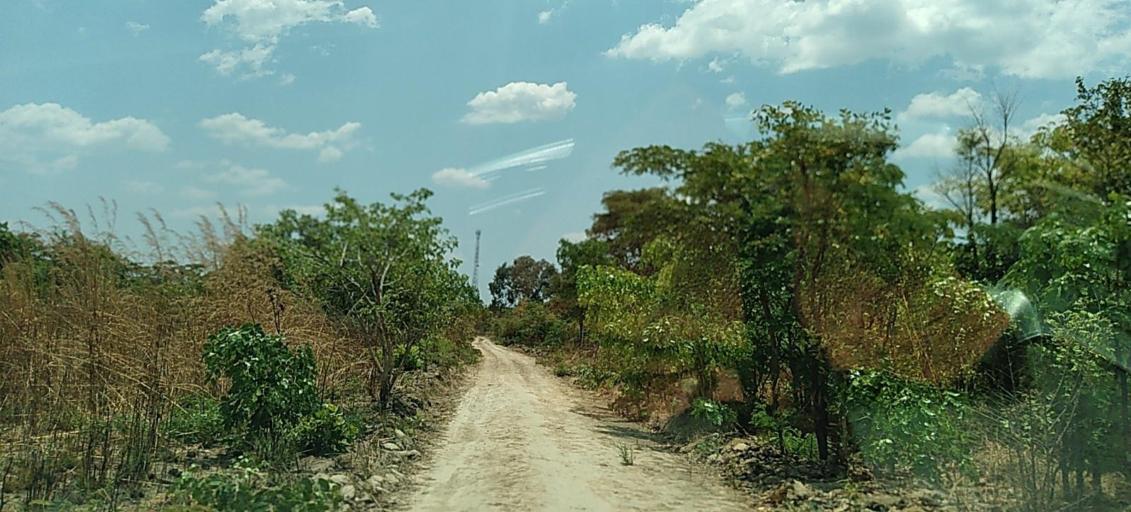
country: ZM
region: Copperbelt
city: Chililabombwe
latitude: -12.4519
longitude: 27.6772
